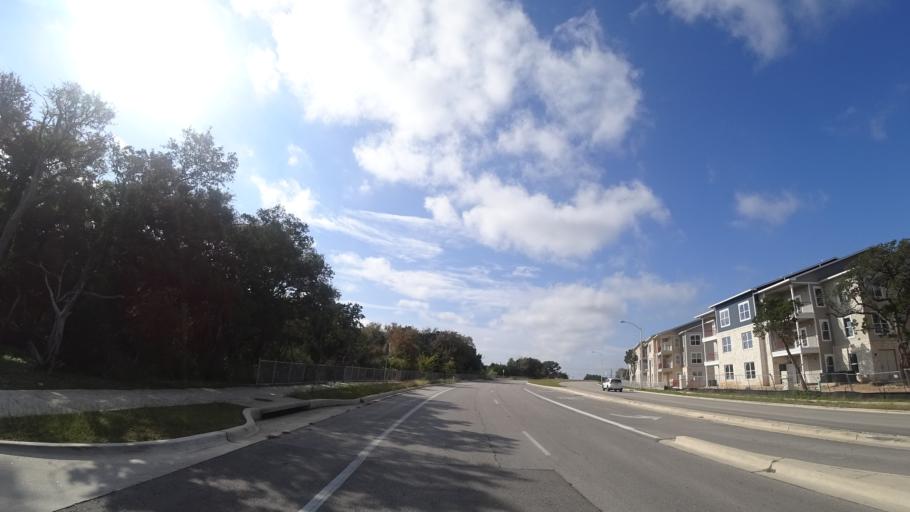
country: US
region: Texas
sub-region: Travis County
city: Shady Hollow
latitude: 30.1930
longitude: -97.8315
